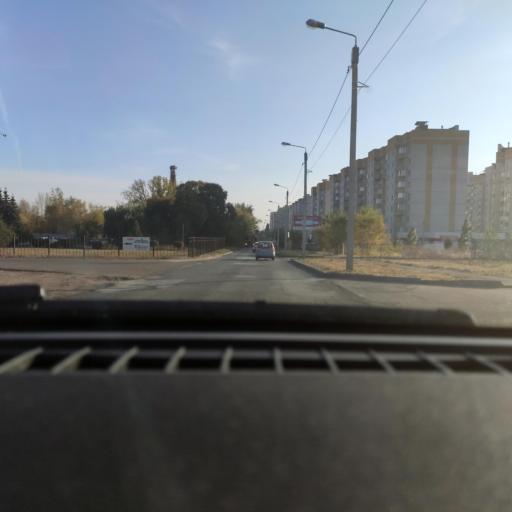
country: RU
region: Voronezj
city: Somovo
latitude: 51.6773
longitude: 39.2915
